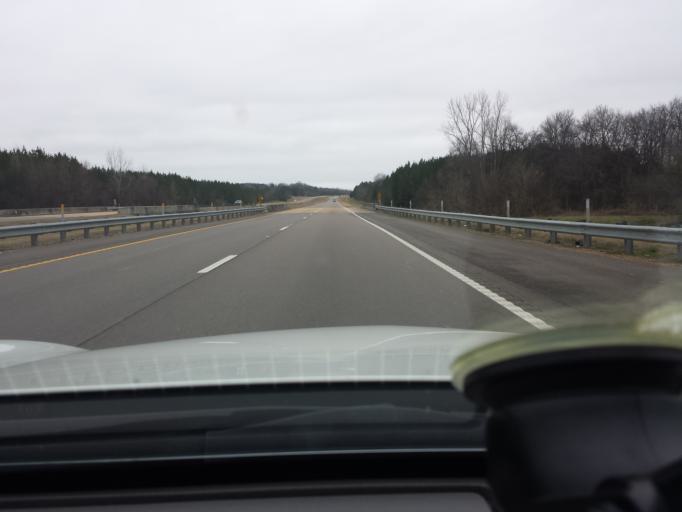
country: US
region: Mississippi
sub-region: Lee County
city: Shannon
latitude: 34.0975
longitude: -88.7007
